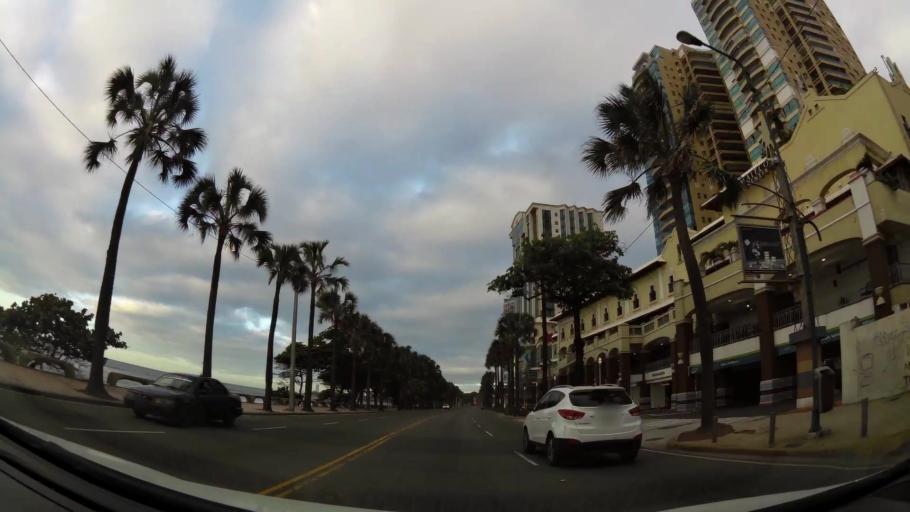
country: DO
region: Nacional
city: Ciudad Nueva
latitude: 18.4581
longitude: -69.9085
